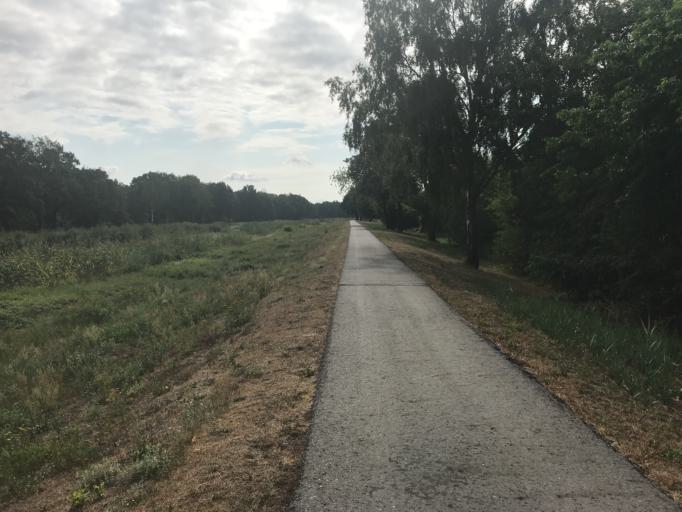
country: DE
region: Brandenburg
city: Schilda
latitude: 51.5840
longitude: 13.3353
